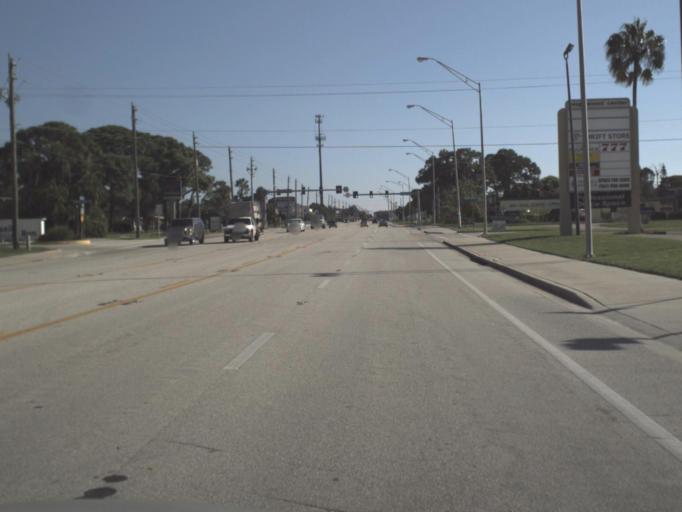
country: US
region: Florida
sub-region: Sarasota County
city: Englewood
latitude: 26.9573
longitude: -82.3532
